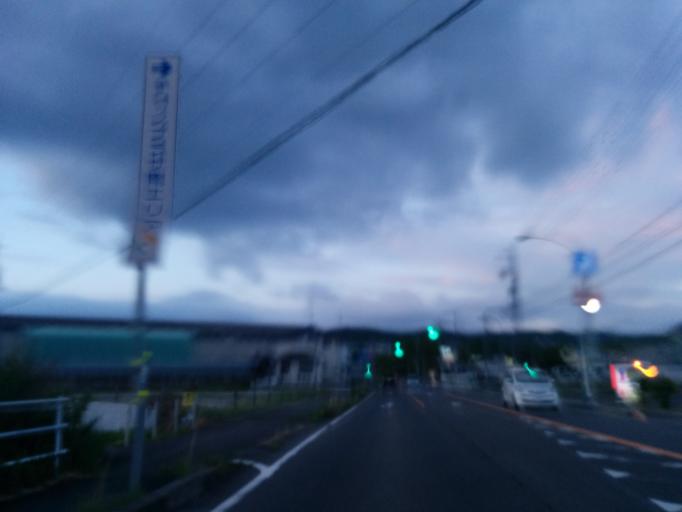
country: JP
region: Gifu
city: Kakamigahara
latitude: 35.4236
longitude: 136.8848
